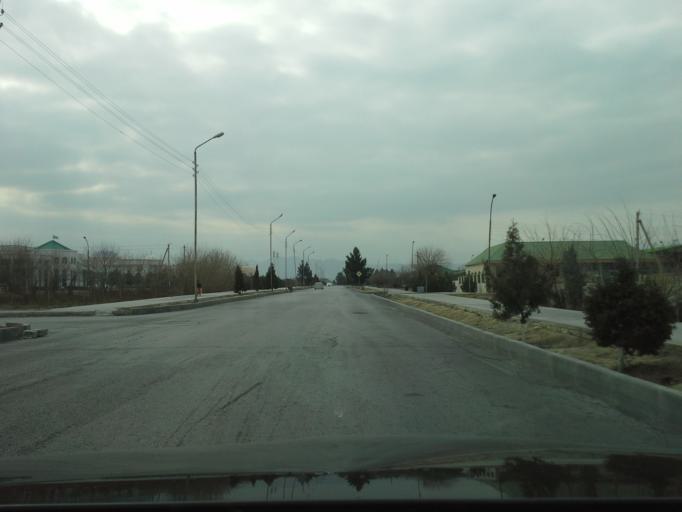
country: TM
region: Ahal
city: Abadan
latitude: 38.0299
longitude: 58.2641
